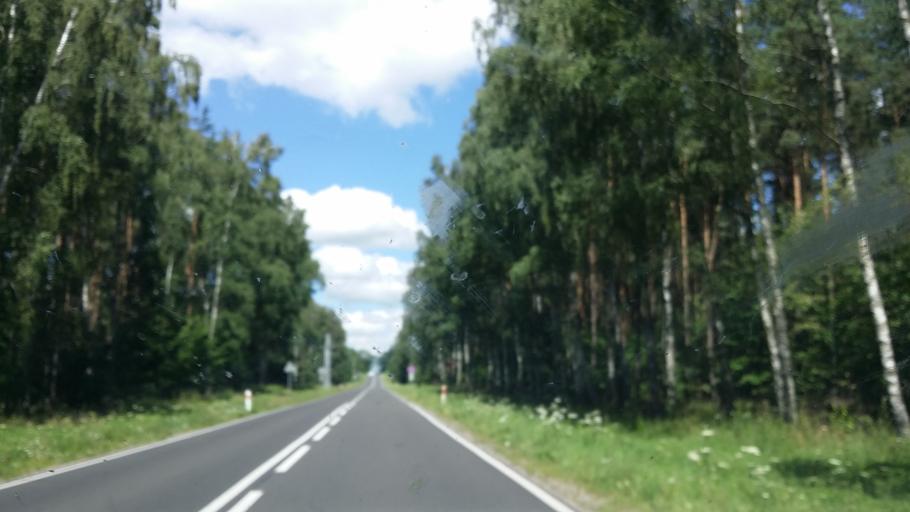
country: PL
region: West Pomeranian Voivodeship
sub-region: Powiat swidwinski
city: Slawoborze
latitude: 53.8779
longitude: 15.7270
